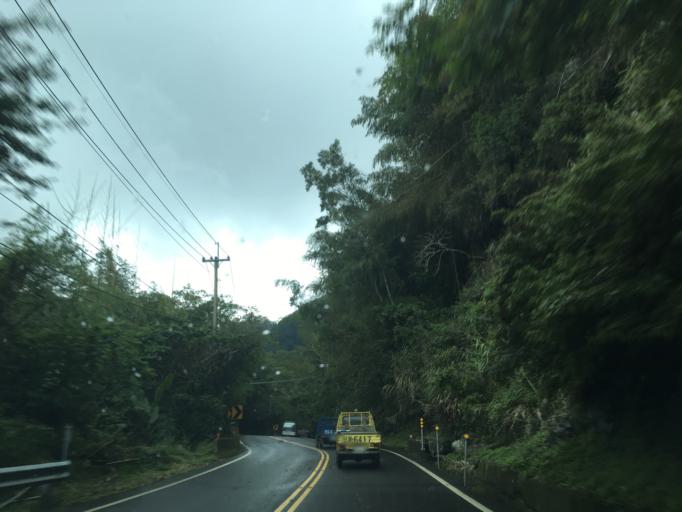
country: TW
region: Taiwan
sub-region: Chiayi
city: Jiayi Shi
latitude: 23.4541
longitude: 120.6800
